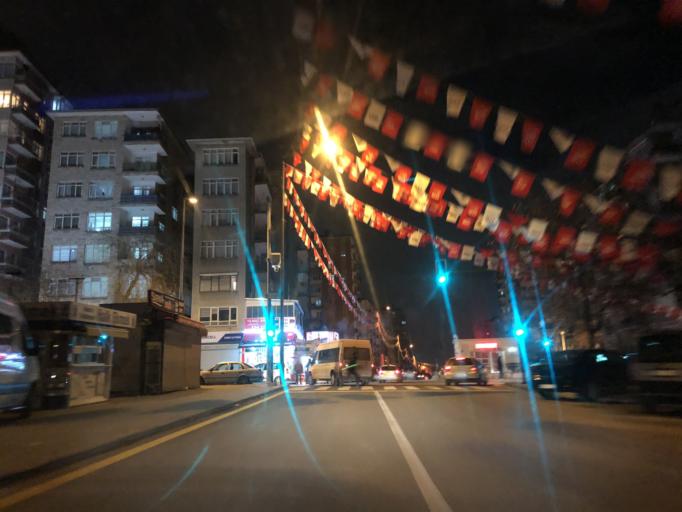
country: TR
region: Ankara
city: Batikent
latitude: 39.9661
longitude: 32.7923
